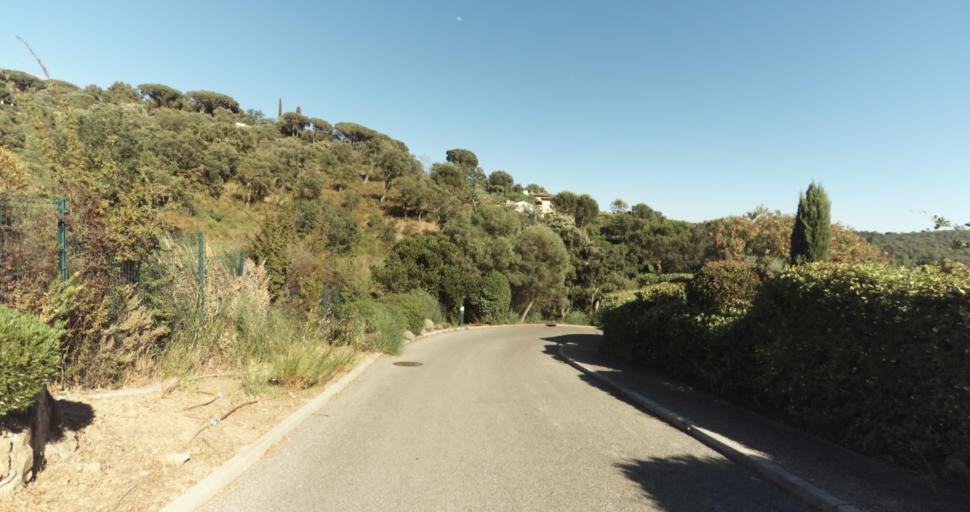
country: FR
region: Provence-Alpes-Cote d'Azur
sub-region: Departement du Var
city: Gassin
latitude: 43.2572
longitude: 6.6060
